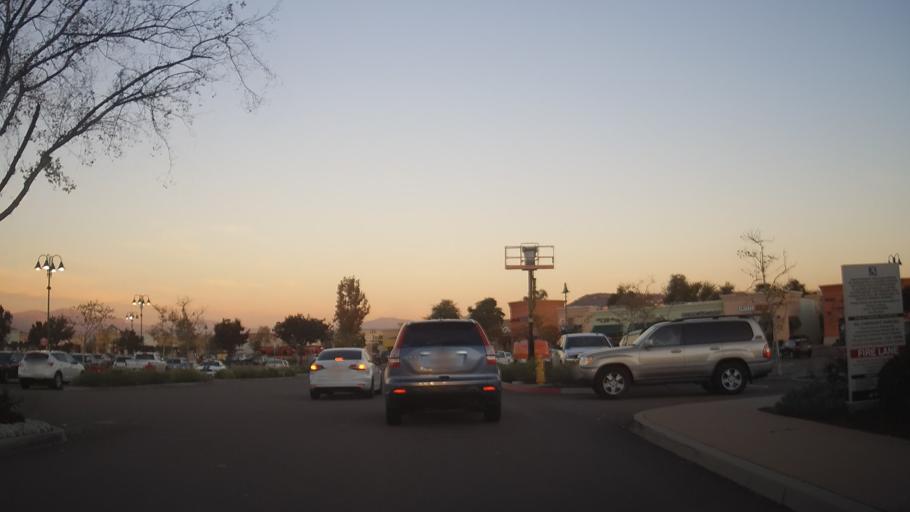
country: US
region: California
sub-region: San Diego County
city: Santee
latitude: 32.8410
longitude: -116.9834
